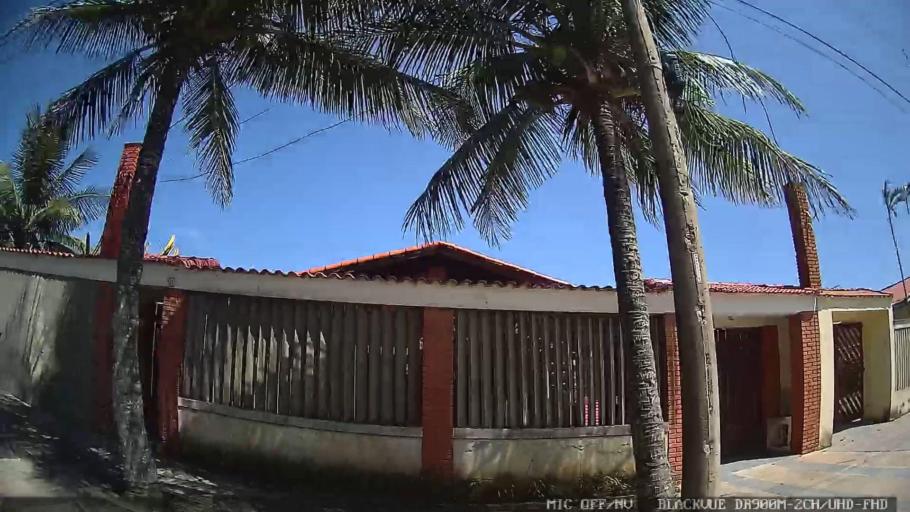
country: BR
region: Sao Paulo
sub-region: Peruibe
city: Peruibe
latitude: -24.3033
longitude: -46.9719
